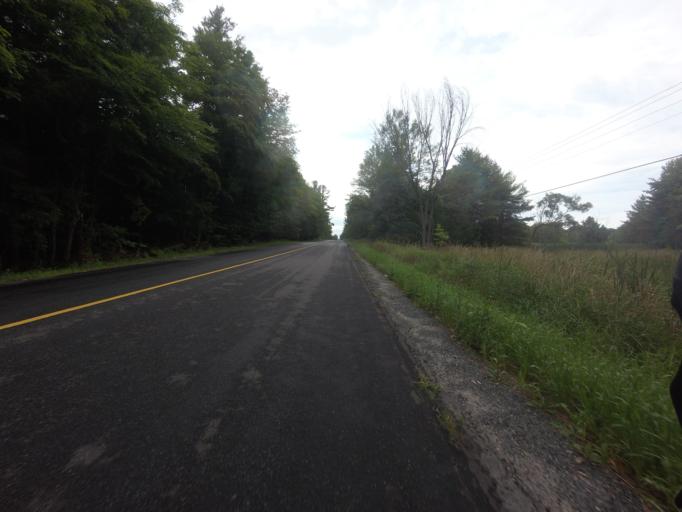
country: CA
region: Ontario
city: Perth
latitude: 45.0731
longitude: -76.3888
